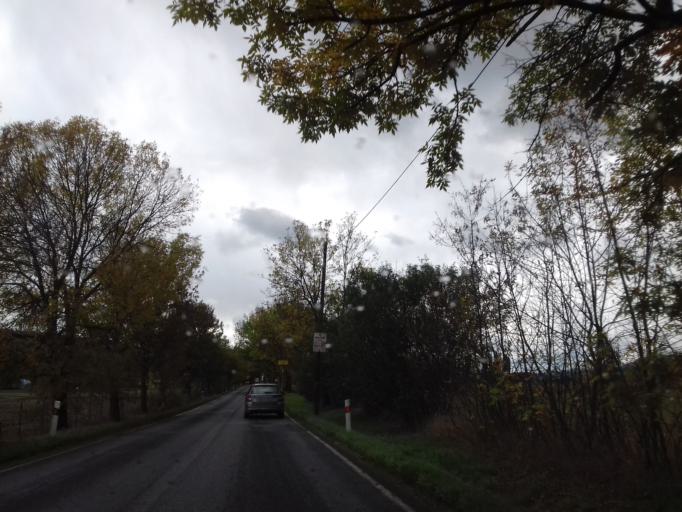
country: CZ
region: Central Bohemia
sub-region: Okres Praha-Zapad
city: Dobrichovice
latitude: 49.9388
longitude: 14.2873
